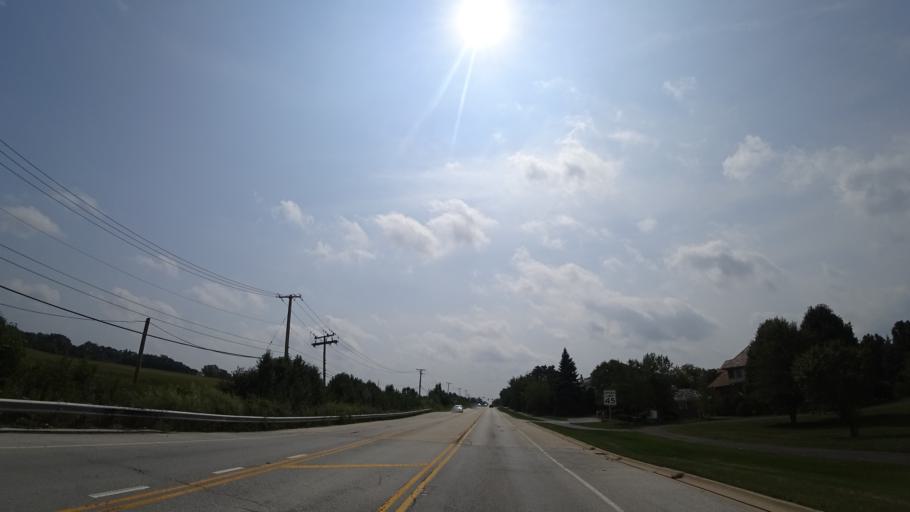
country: US
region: Illinois
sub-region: Cook County
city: Orland Park
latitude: 41.6144
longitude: -87.8919
